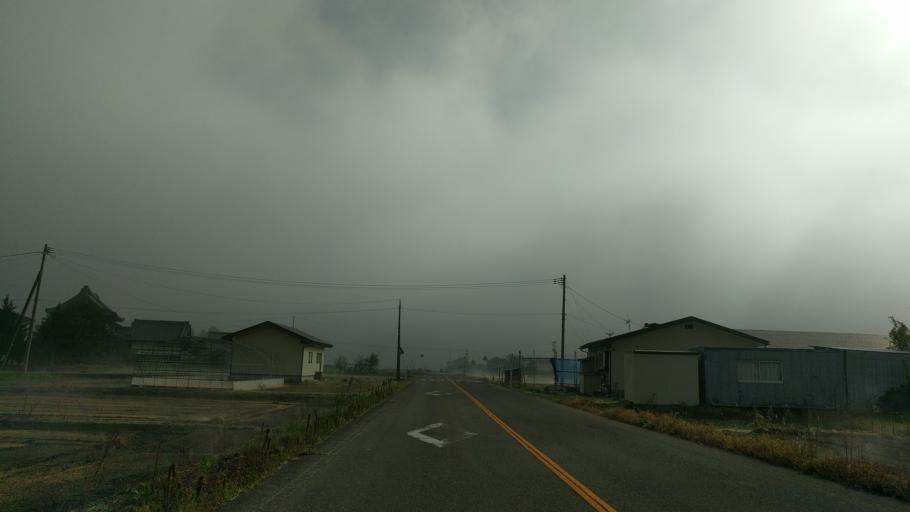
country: JP
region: Fukushima
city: Kitakata
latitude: 37.5041
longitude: 139.8462
